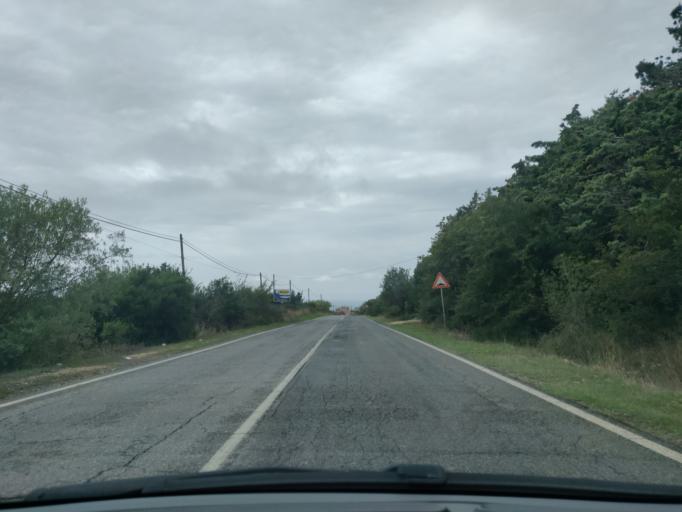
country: IT
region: Latium
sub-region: Citta metropolitana di Roma Capitale
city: Civitavecchia
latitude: 42.1086
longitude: 11.8400
